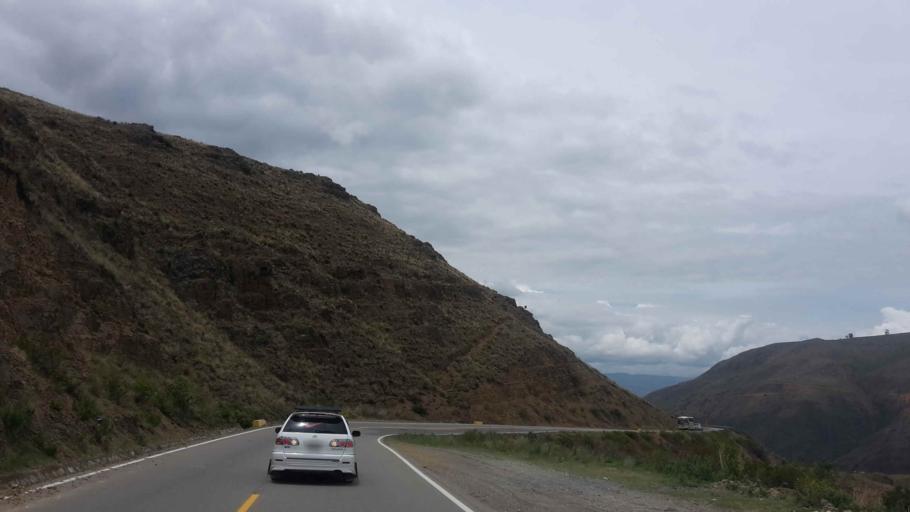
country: BO
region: Cochabamba
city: Punata
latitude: -17.4822
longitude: -65.7777
